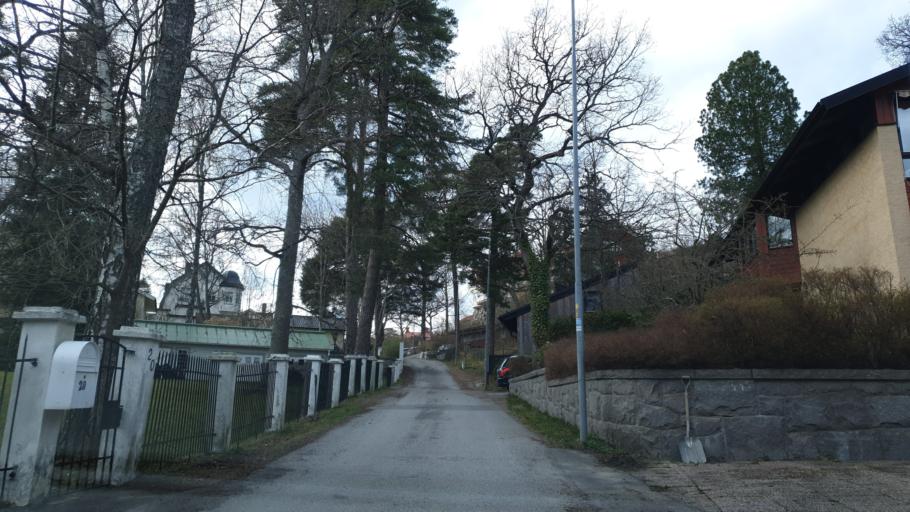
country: SE
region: Stockholm
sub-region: Nacka Kommun
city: Saltsjobaden
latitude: 59.2773
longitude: 18.3084
